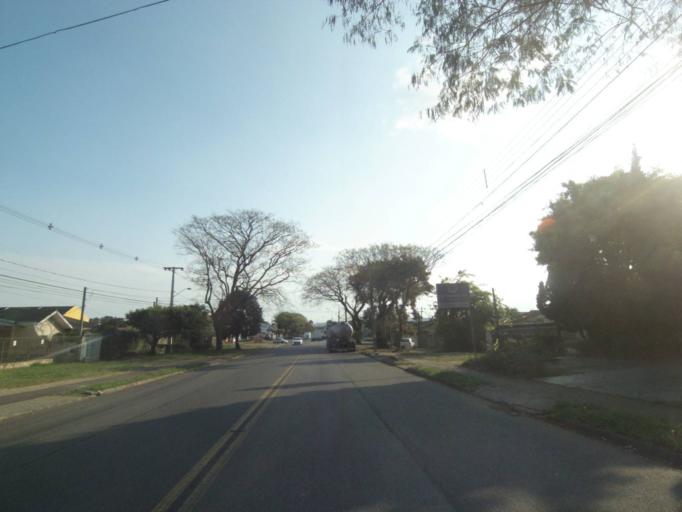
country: BR
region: Parana
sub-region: Curitiba
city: Curitiba
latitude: -25.4881
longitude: -49.3311
